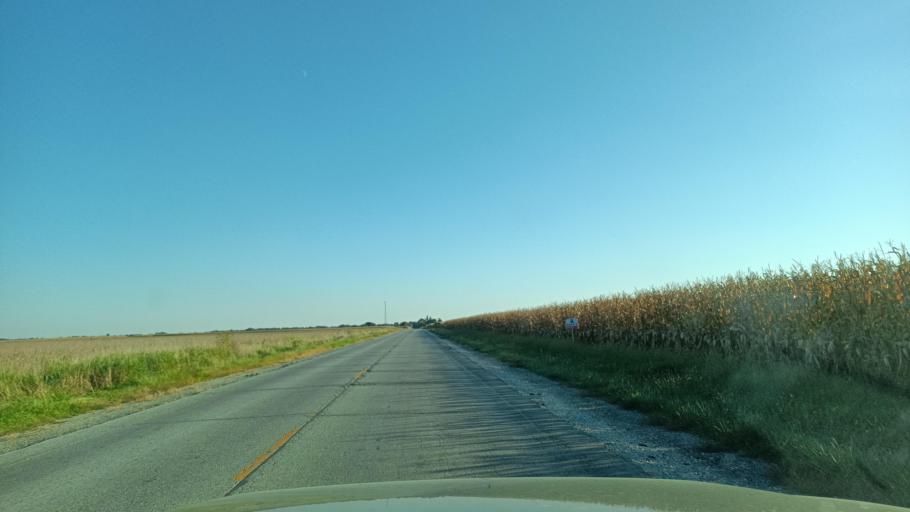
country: US
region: Illinois
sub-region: Warren County
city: Monmouth
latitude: 41.0177
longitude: -90.6276
